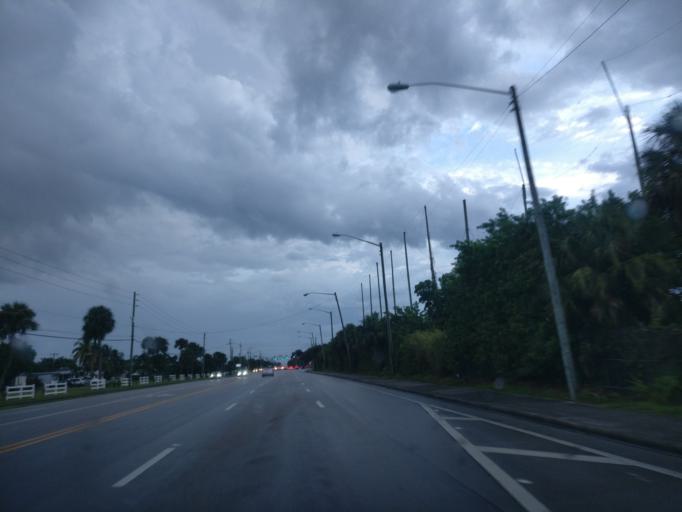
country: US
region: Florida
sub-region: Palm Beach County
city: Schall Circle
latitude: 26.7105
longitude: -80.1193
